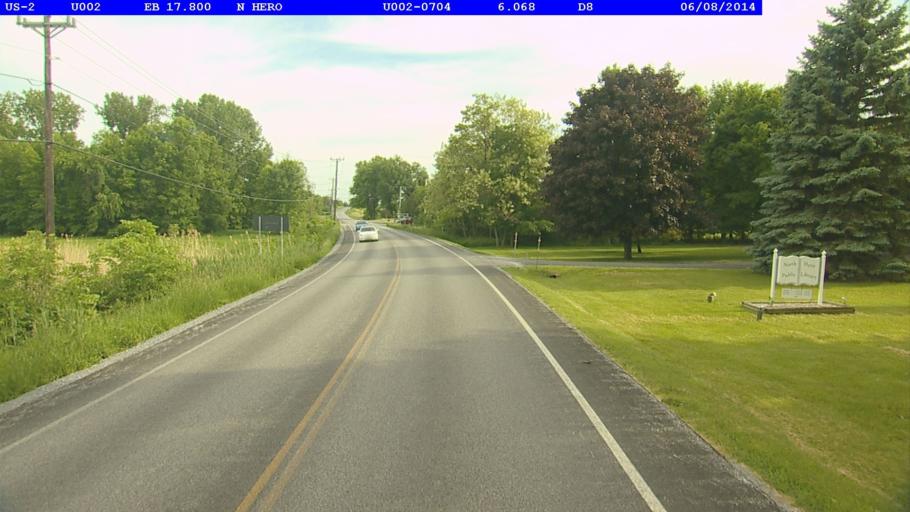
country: US
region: Vermont
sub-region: Grand Isle County
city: North Hero
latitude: 44.8119
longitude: -73.2921
